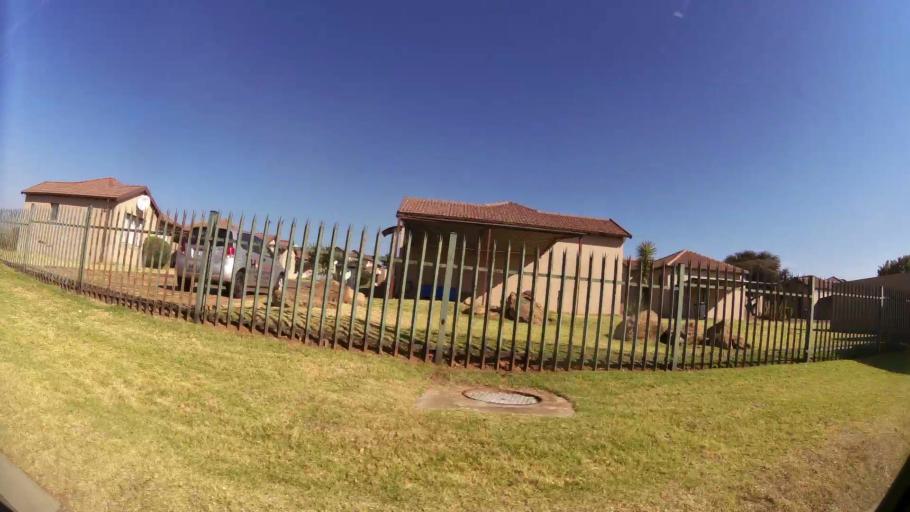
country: ZA
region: Gauteng
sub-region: Ekurhuleni Metropolitan Municipality
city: Germiston
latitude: -26.2468
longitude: 28.1139
